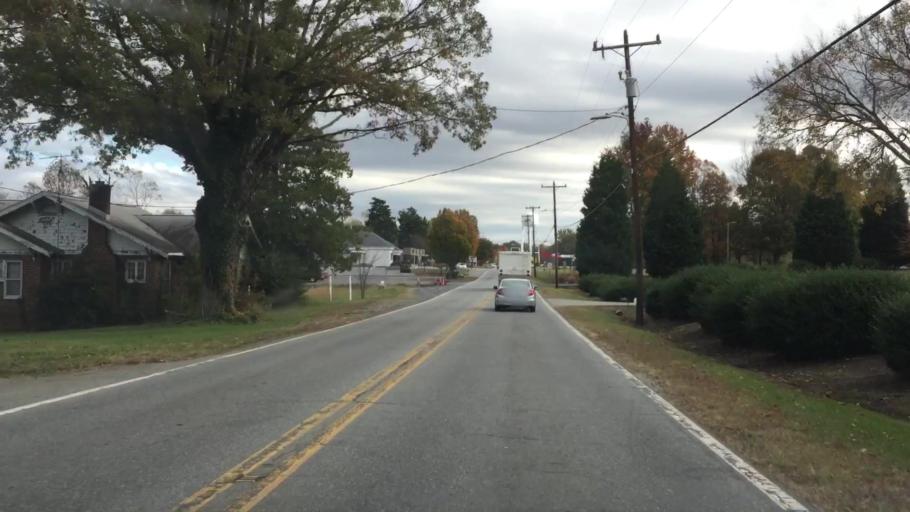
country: US
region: North Carolina
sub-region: Guilford County
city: Stokesdale
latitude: 36.2405
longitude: -79.9830
